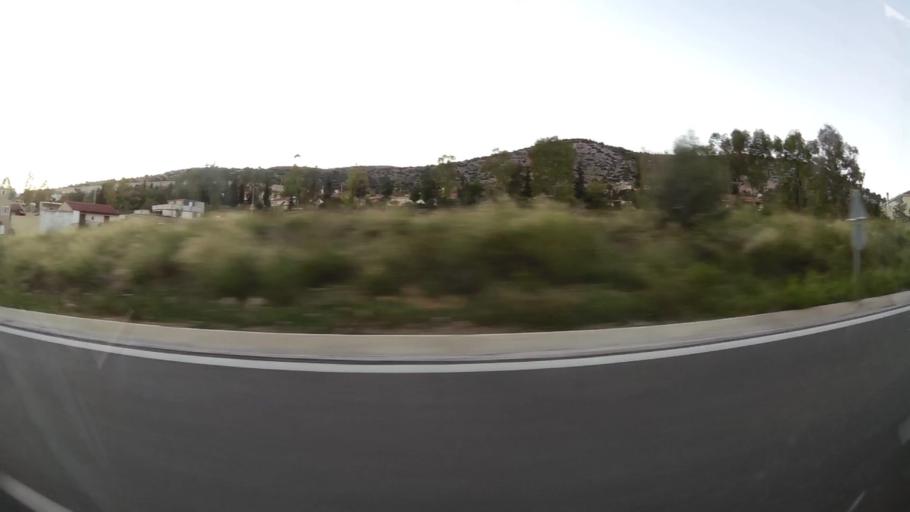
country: GR
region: Attica
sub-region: Nomarchia Dytikis Attikis
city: Ano Liosia
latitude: 38.0863
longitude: 23.6817
